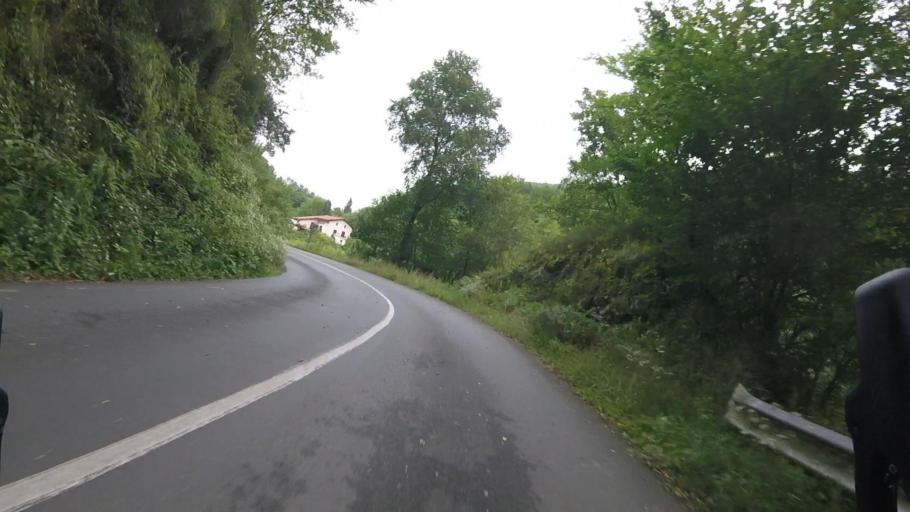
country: ES
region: Basque Country
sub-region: Provincia de Guipuzcoa
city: Irun
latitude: 43.2823
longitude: -1.8207
